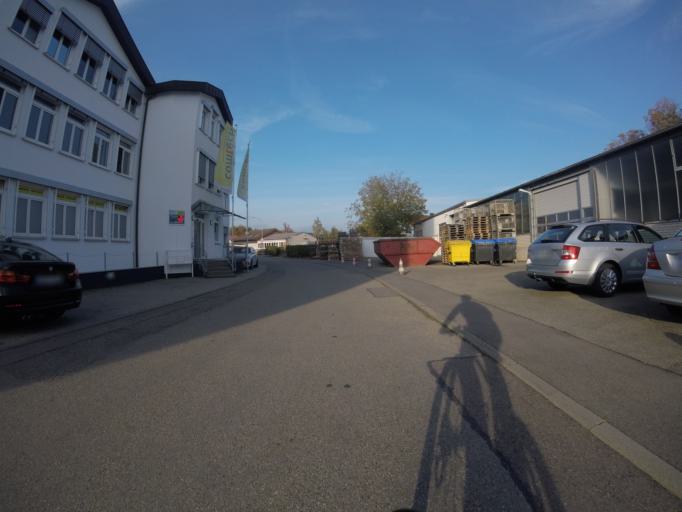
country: DE
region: Baden-Wuerttemberg
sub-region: Regierungsbezirk Stuttgart
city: Aspach
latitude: 48.9726
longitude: 9.4003
